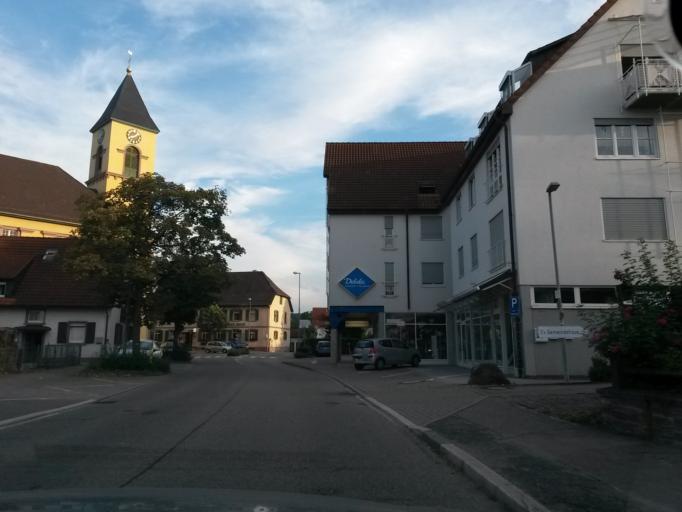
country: DE
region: Baden-Wuerttemberg
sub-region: Karlsruhe Region
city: Ettlingen
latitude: 48.9176
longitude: 8.5055
